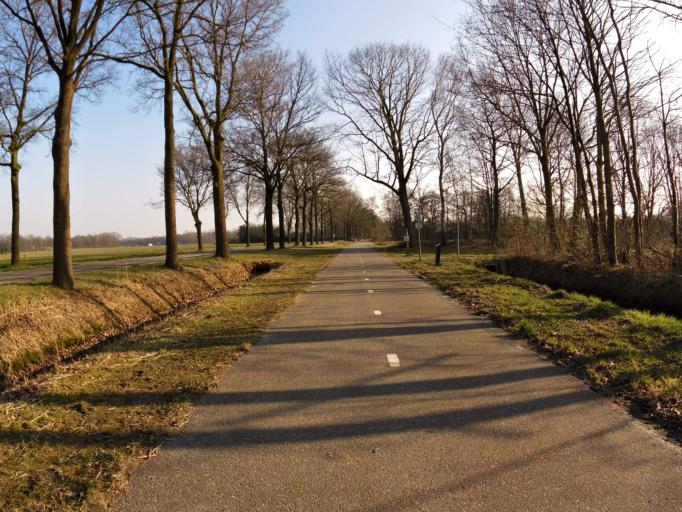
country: NL
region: North Brabant
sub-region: Gemeente Maasdonk
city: Geffen
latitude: 51.7052
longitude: 5.4382
